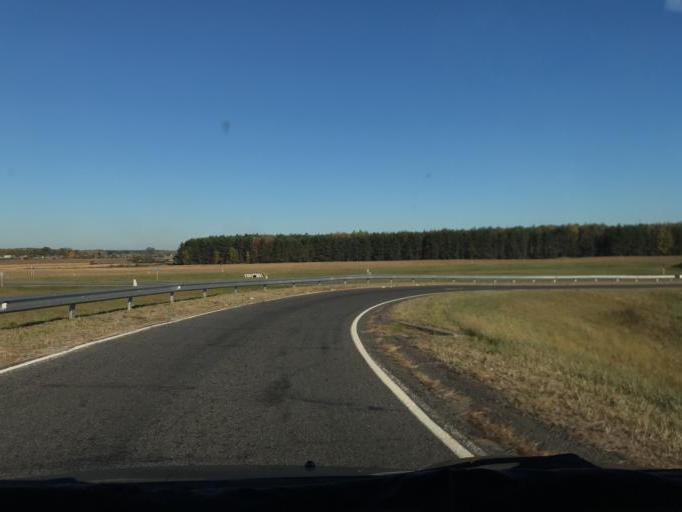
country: BY
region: Gomel
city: Kalinkavichy
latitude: 52.0745
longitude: 29.3599
